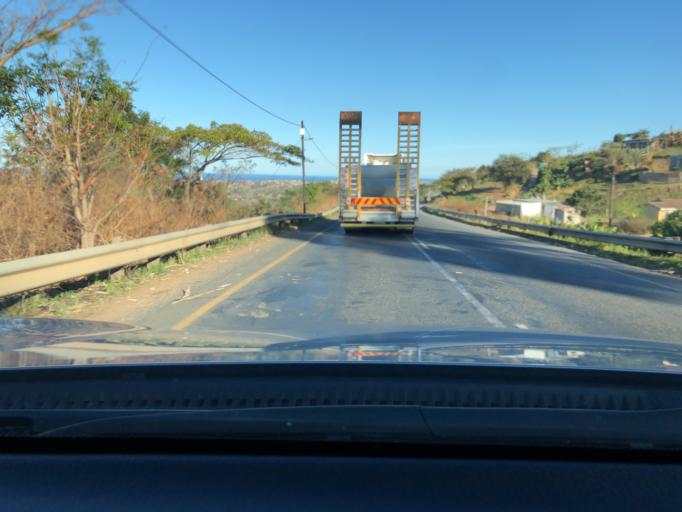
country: ZA
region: KwaZulu-Natal
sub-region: eThekwini Metropolitan Municipality
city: Umkomaas
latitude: -30.0218
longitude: 30.8107
